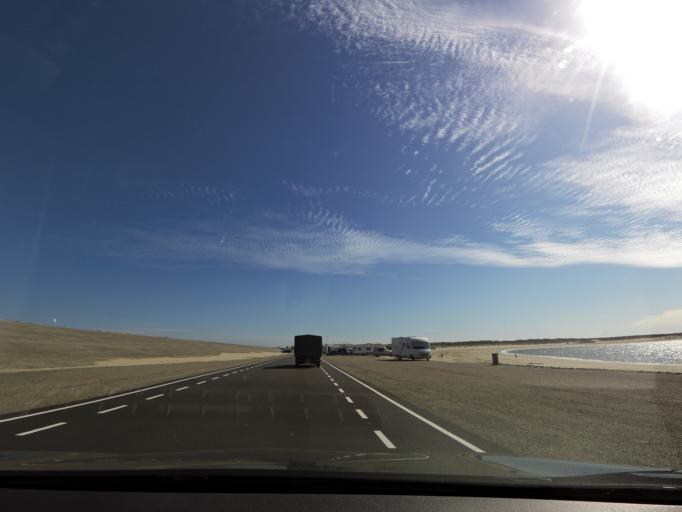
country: NL
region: Zeeland
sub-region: Schouwen-Duiveland
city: Scharendijke
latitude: 51.7460
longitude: 3.8246
